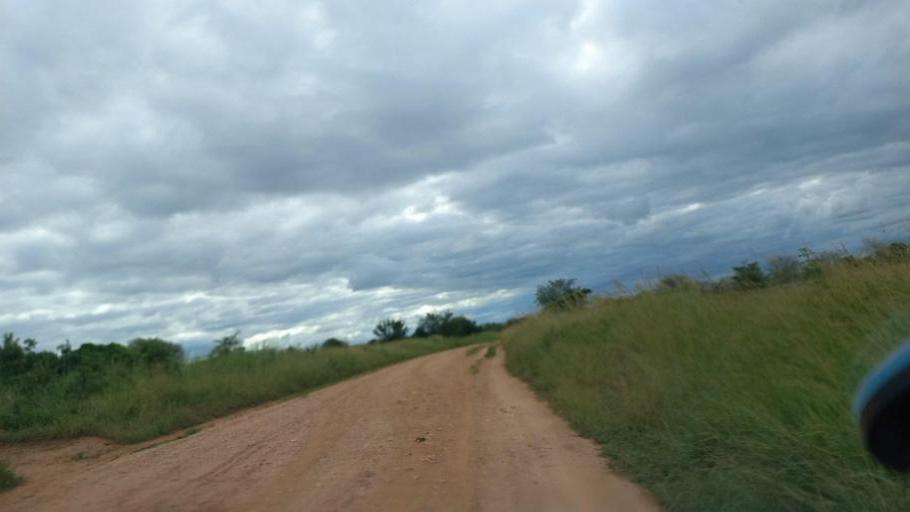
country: ZM
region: Lusaka
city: Chongwe
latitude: -15.4513
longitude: 28.8290
